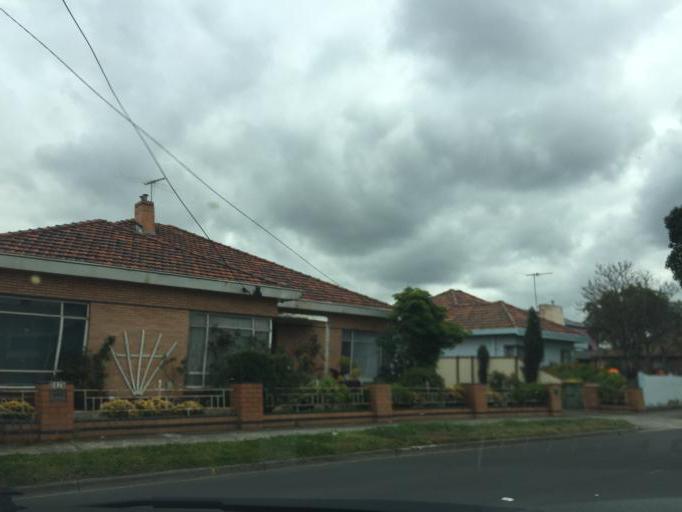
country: AU
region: Victoria
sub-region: Maribyrnong
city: Kingsville
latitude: -37.8188
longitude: 144.8823
